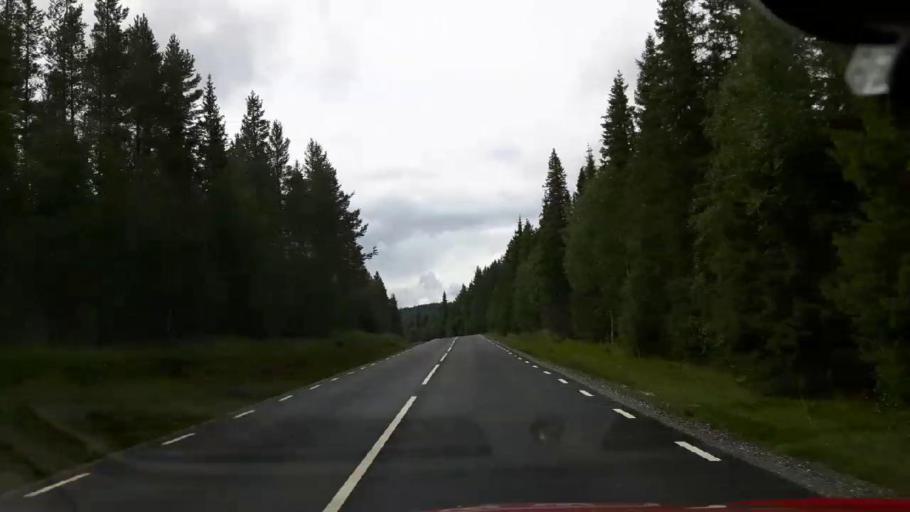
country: NO
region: Nord-Trondelag
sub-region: Lierne
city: Sandvika
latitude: 64.6290
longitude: 14.1282
